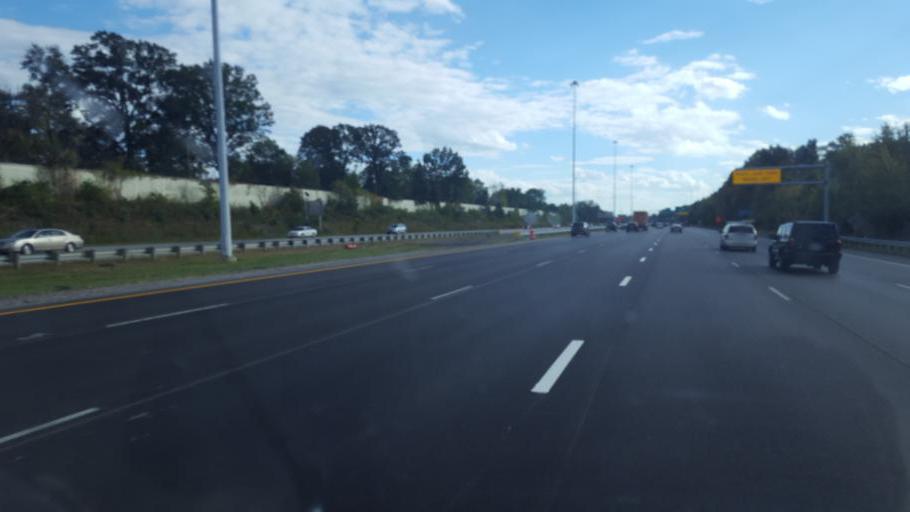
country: US
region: Ohio
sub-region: Franklin County
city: Gahanna
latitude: 40.0293
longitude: -82.9038
